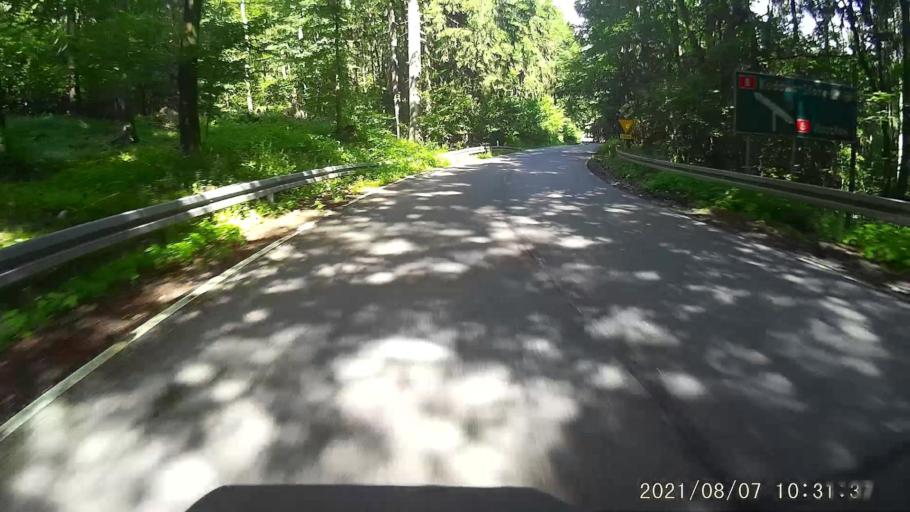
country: PL
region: Lower Silesian Voivodeship
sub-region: Powiat klodzki
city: Duszniki-Zdroj
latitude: 50.3951
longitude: 16.3537
